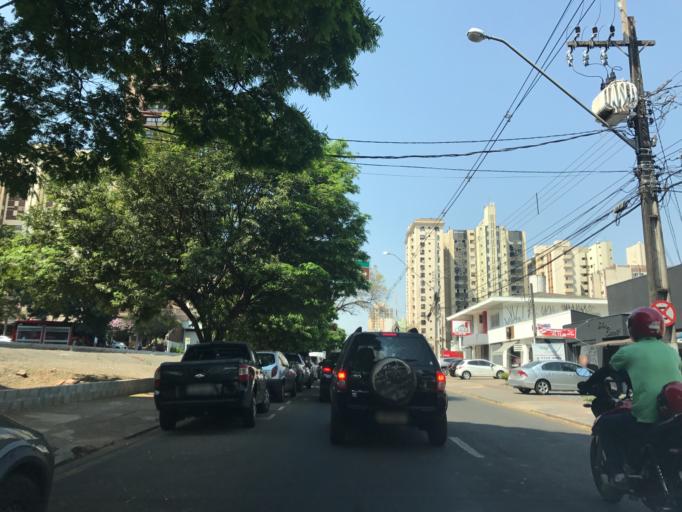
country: BR
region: Parana
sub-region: Londrina
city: Londrina
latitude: -23.3155
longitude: -51.1665
